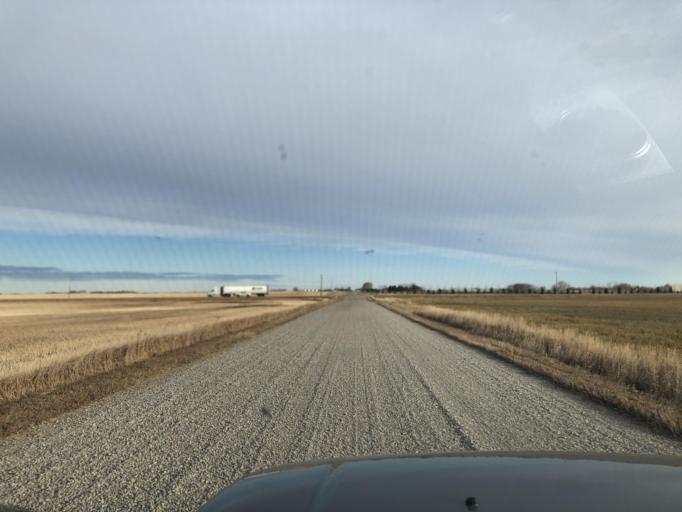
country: CA
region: Alberta
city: Strathmore
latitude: 50.8926
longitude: -113.5399
